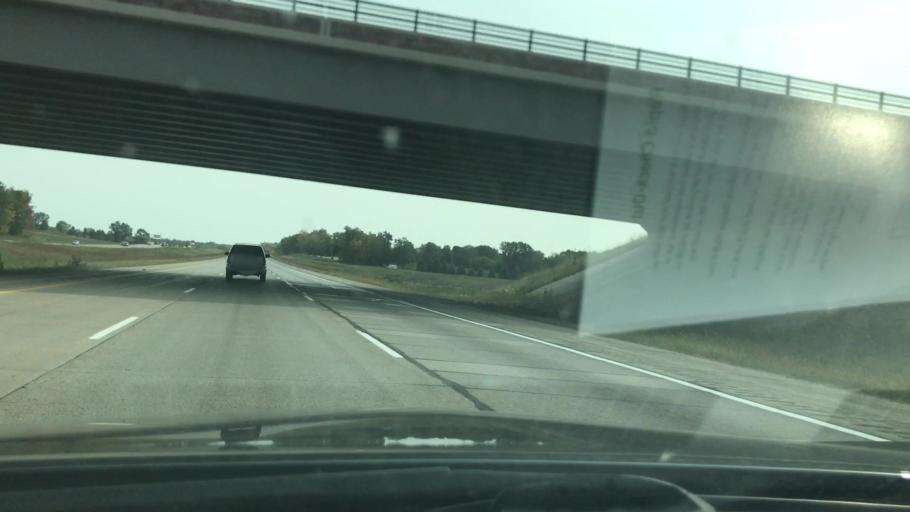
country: US
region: Michigan
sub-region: Livingston County
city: Howell
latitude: 42.5784
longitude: -83.8745
